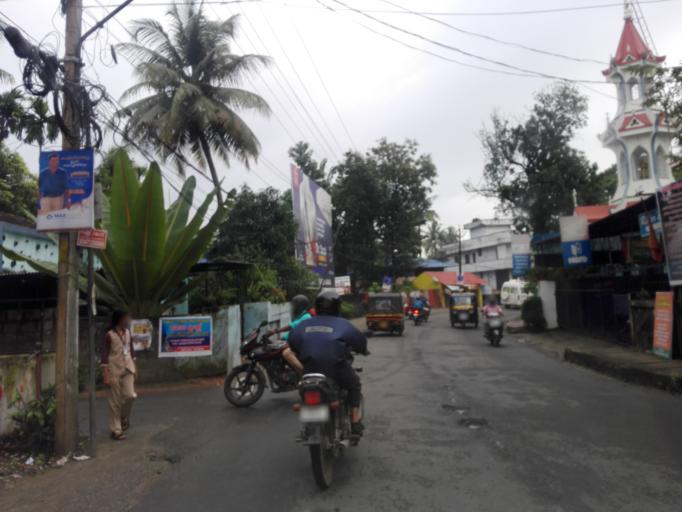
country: IN
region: Kerala
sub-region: Alappuzha
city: Arukutti
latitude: 9.9492
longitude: 76.3552
